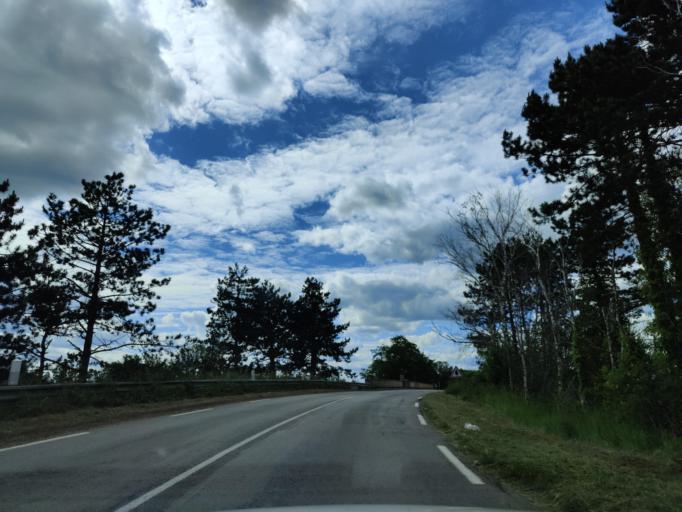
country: FR
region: Ile-de-France
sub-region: Departement de l'Essonne
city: Boissy-sous-Saint-Yon
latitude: 48.5589
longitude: 2.2261
